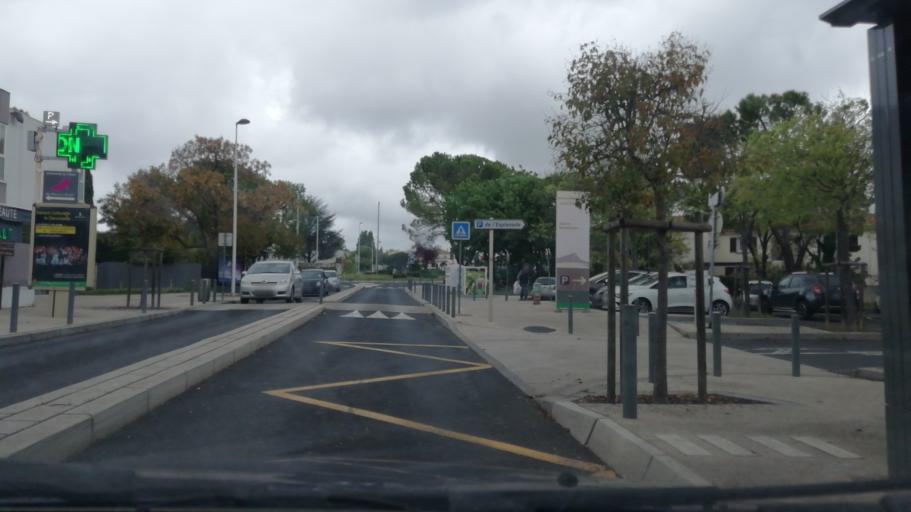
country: FR
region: Languedoc-Roussillon
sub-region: Departement de l'Herault
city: Saint-Gely-du-Fesc
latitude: 43.6937
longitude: 3.8069
